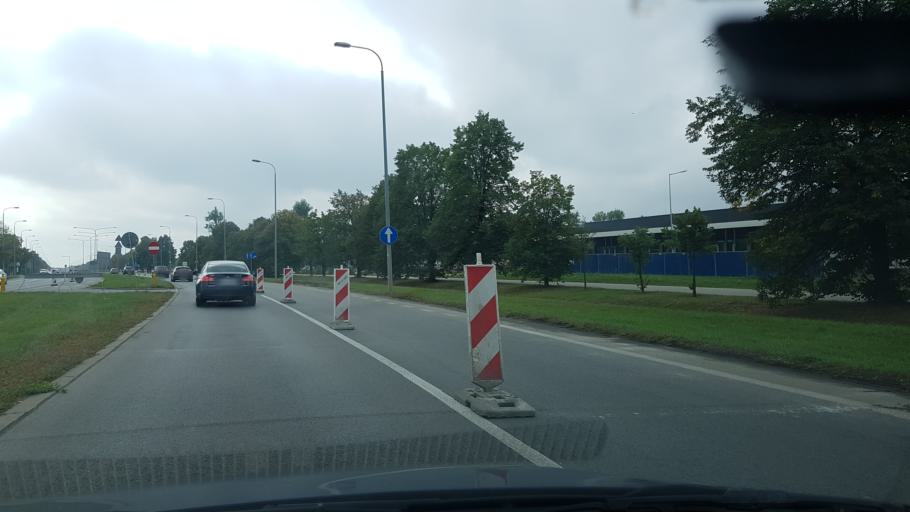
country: PL
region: Masovian Voivodeship
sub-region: Warszawa
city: Wilanow
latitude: 52.1492
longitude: 21.0922
